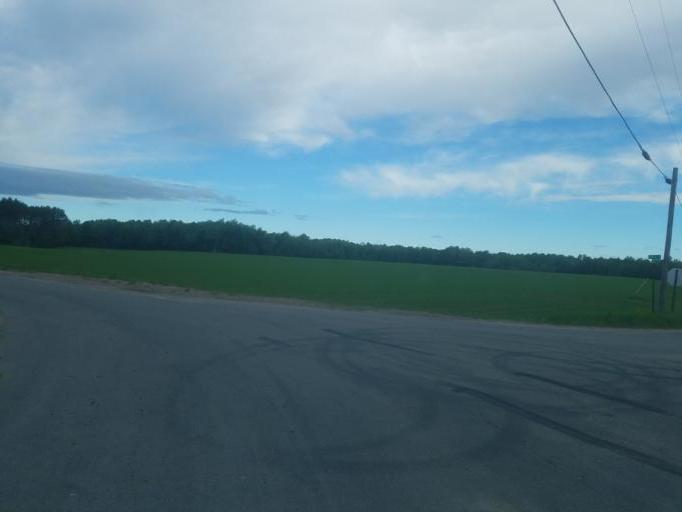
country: US
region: New York
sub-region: Herkimer County
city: Herkimer
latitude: 43.2617
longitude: -74.9811
